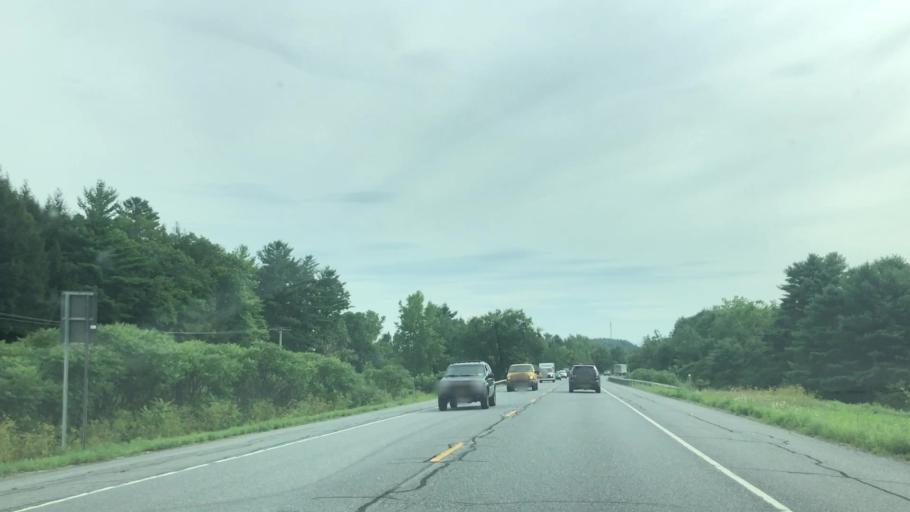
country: US
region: New York
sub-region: Washington County
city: Whitehall
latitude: 43.4342
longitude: -73.4625
